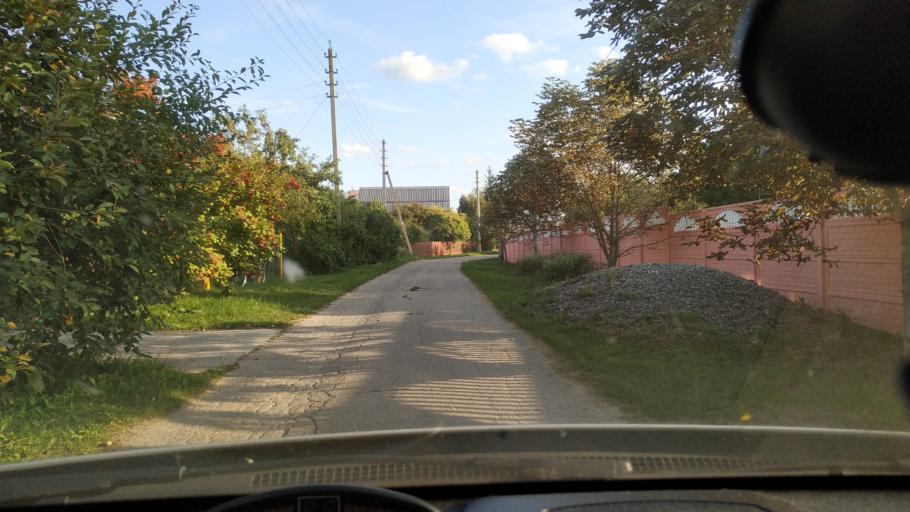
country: RU
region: Rjazan
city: Solotcha
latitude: 54.8686
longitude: 39.6699
